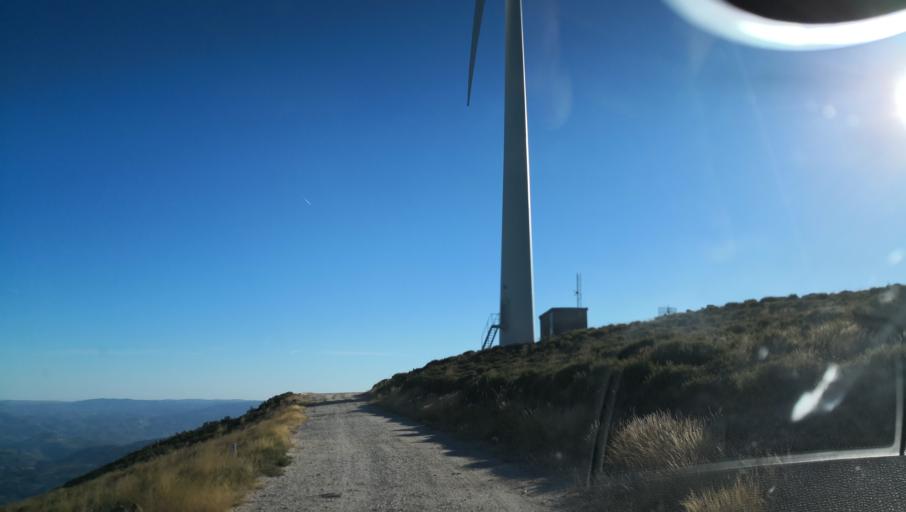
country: PT
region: Vila Real
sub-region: Vila Real
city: Vila Real
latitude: 41.3547
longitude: -7.7710
